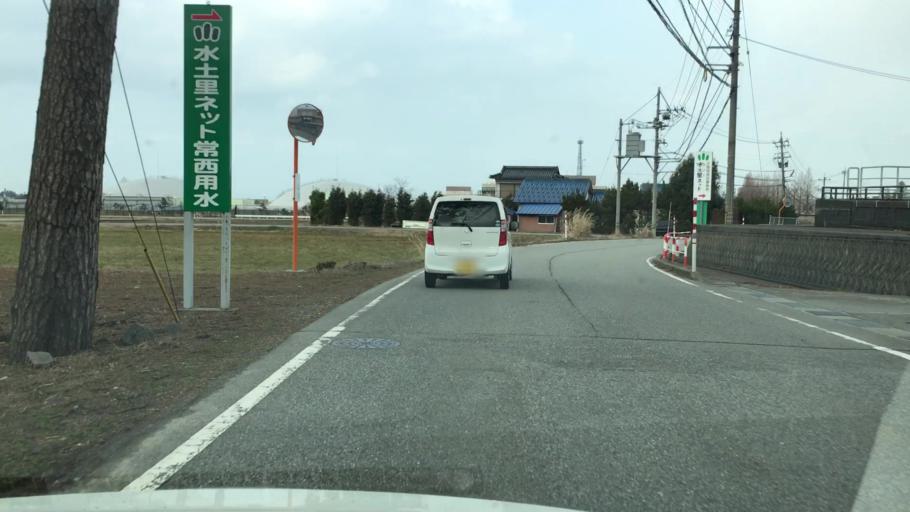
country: JP
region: Toyama
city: Toyama-shi
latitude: 36.6541
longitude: 137.2773
